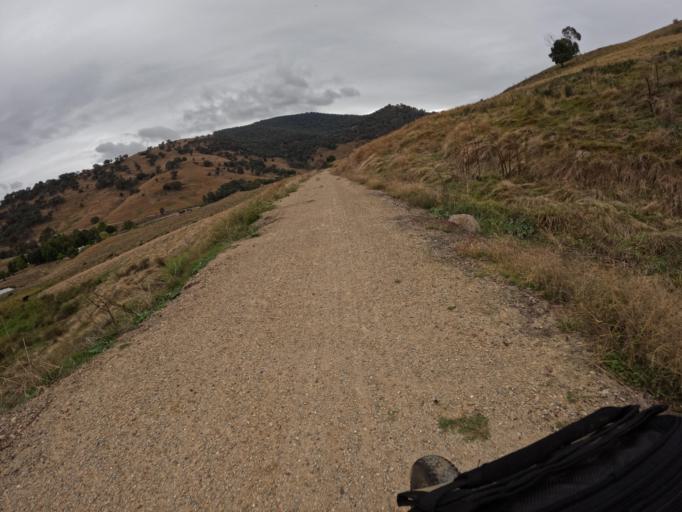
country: AU
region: New South Wales
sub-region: Albury Municipality
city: East Albury
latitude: -36.1845
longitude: 147.3672
